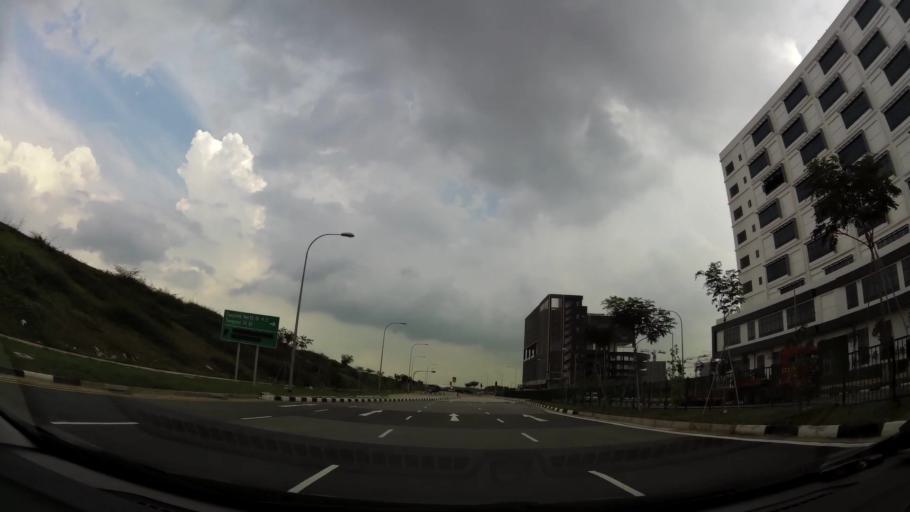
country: SG
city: Singapore
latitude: 1.3662
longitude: 103.9317
